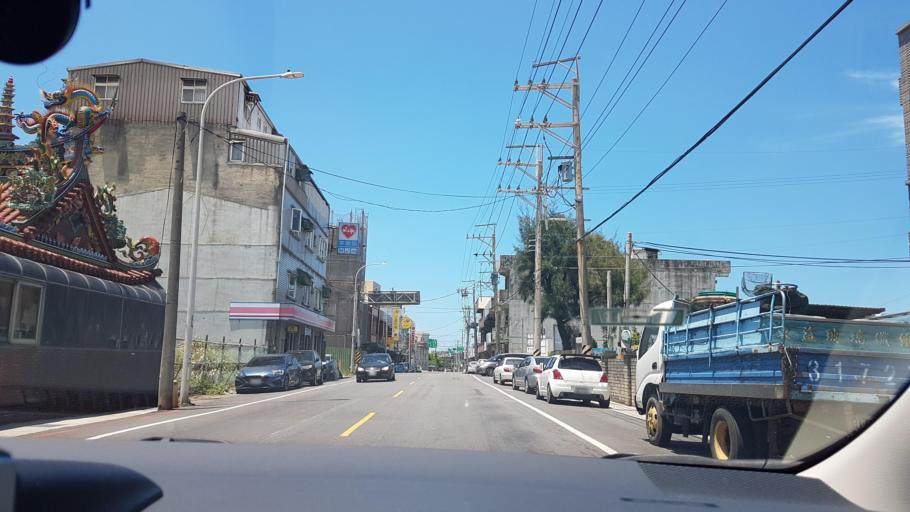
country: TW
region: Taiwan
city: Taoyuan City
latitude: 25.1103
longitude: 121.2550
